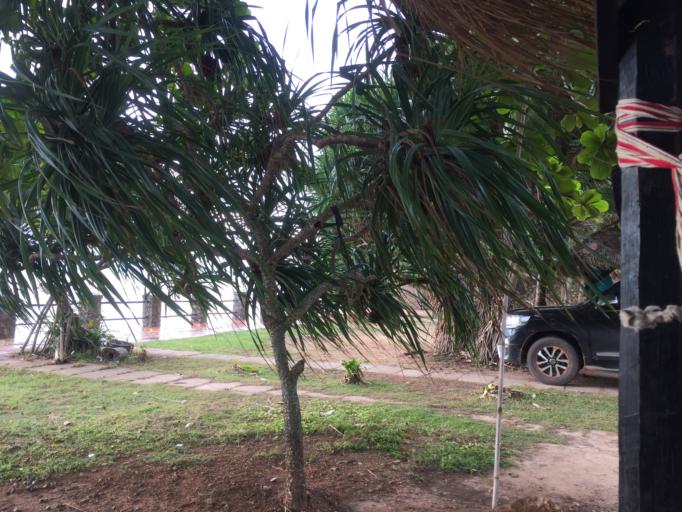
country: KH
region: Kep
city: Krong Kep
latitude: 10.4913
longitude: 104.2893
